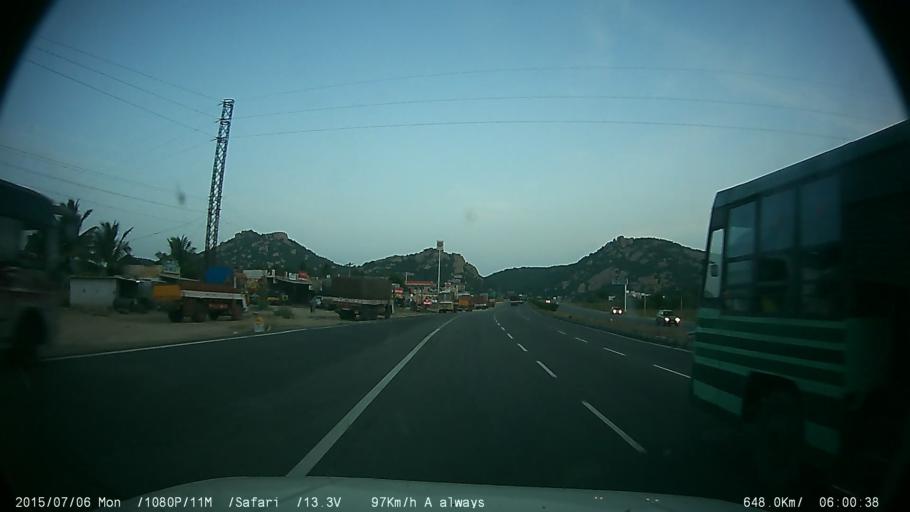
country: IN
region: Tamil Nadu
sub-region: Krishnagiri
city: Krishnagiri
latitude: 12.6013
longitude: 78.1262
